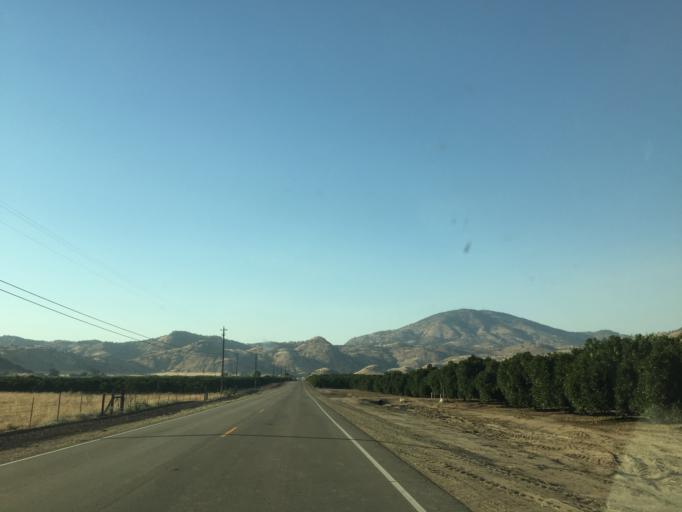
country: US
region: California
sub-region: Fresno County
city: Orange Cove
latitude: 36.6842
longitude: -119.3044
